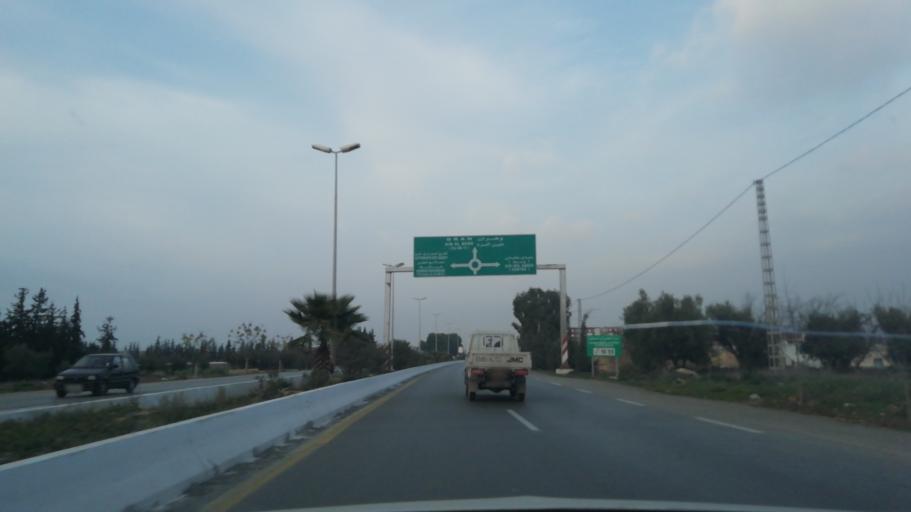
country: DZ
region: Sidi Bel Abbes
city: Sidi Bel Abbes
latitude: 35.2083
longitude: -0.6582
